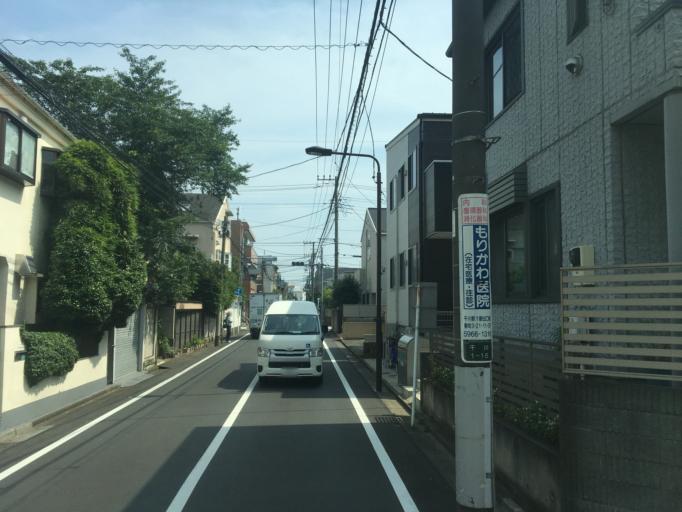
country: JP
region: Tokyo
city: Tokyo
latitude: 35.7389
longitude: 139.6938
